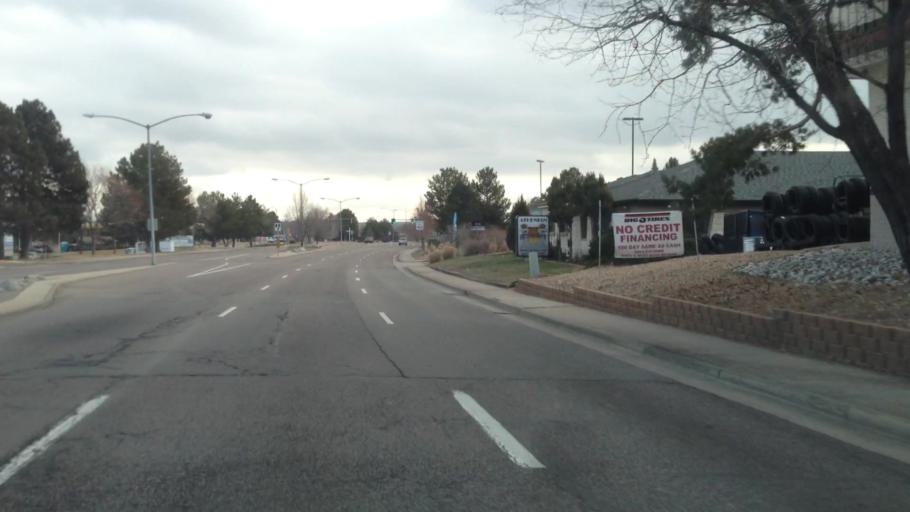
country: US
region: Colorado
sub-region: Adams County
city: Aurora
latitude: 39.6747
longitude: -104.8091
